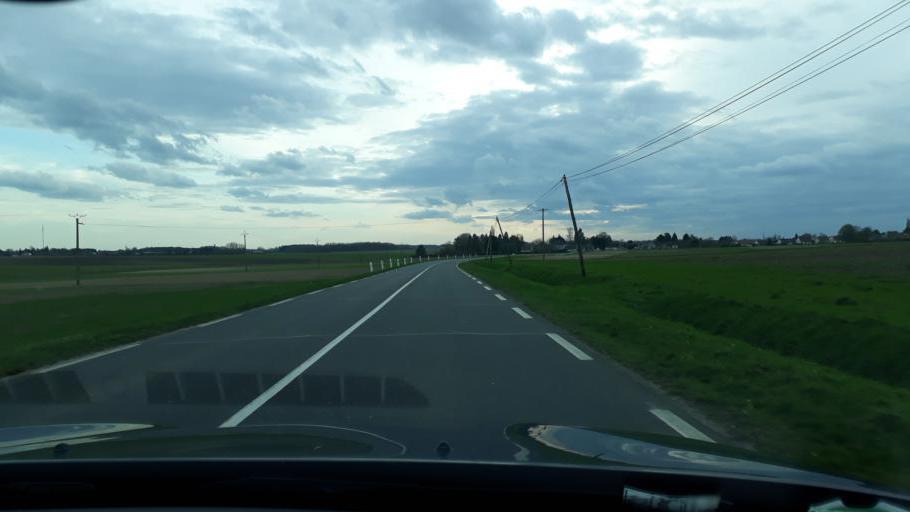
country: FR
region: Centre
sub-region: Departement du Loiret
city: Loury
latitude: 48.0098
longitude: 2.1044
